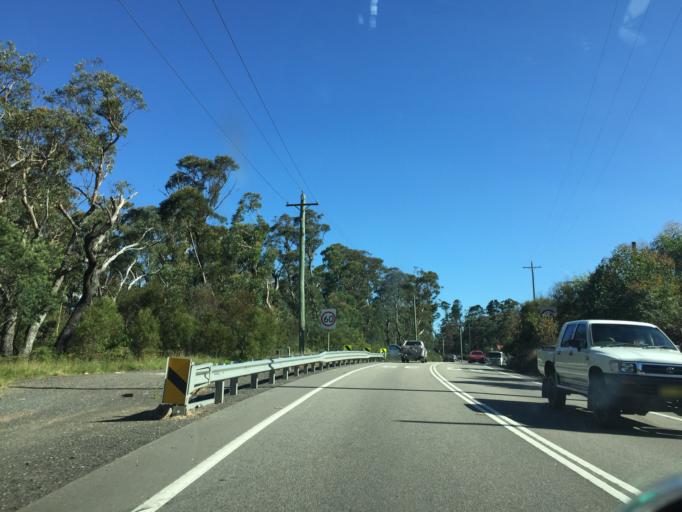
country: AU
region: New South Wales
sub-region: Blue Mountains Municipality
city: Blackheath
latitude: -33.6673
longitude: 150.2801
